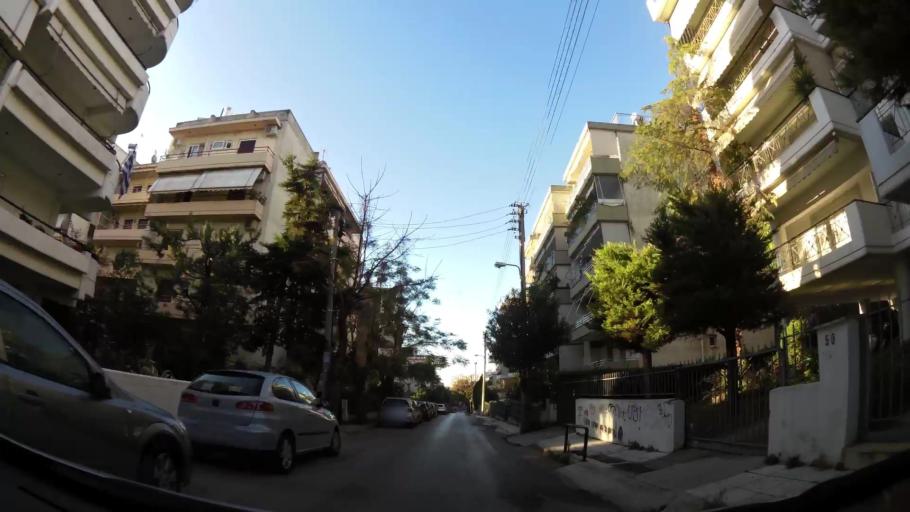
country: GR
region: Attica
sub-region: Nomarchia Athinas
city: Marousi
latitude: 38.0510
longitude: 23.8019
